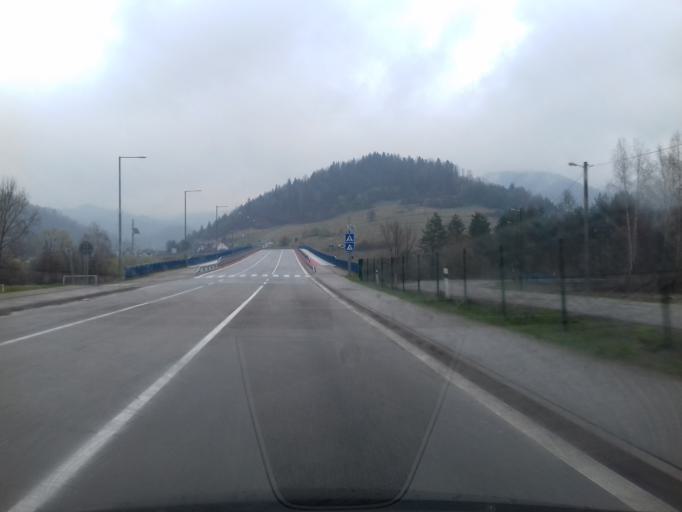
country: PL
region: Lesser Poland Voivodeship
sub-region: Powiat nowosadecki
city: Piwniczna-Zdroj
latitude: 49.4167
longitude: 20.7213
